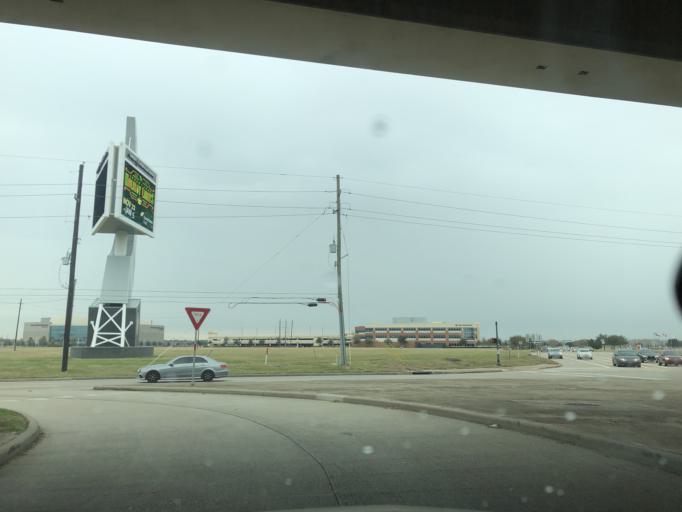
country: US
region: Texas
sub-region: Fort Bend County
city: New Territory
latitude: 29.5809
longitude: -95.6477
